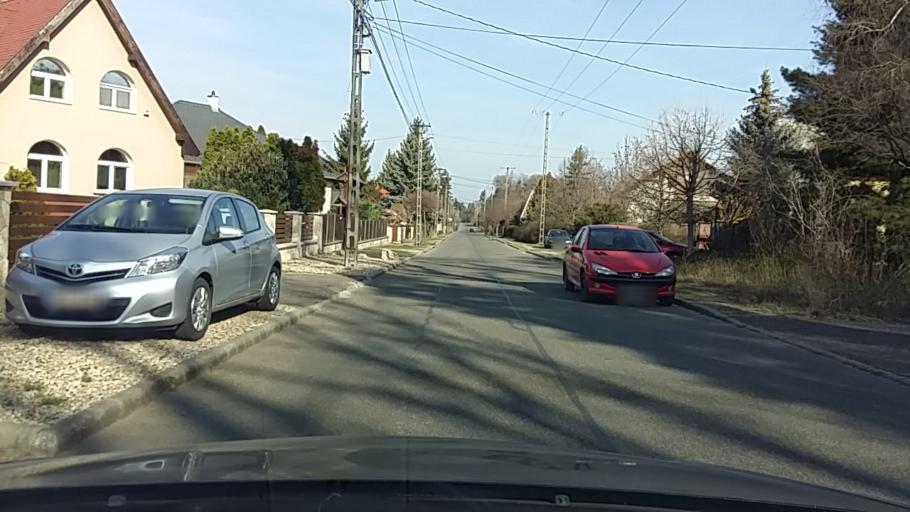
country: HU
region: Pest
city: Godollo
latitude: 47.5840
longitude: 19.3666
